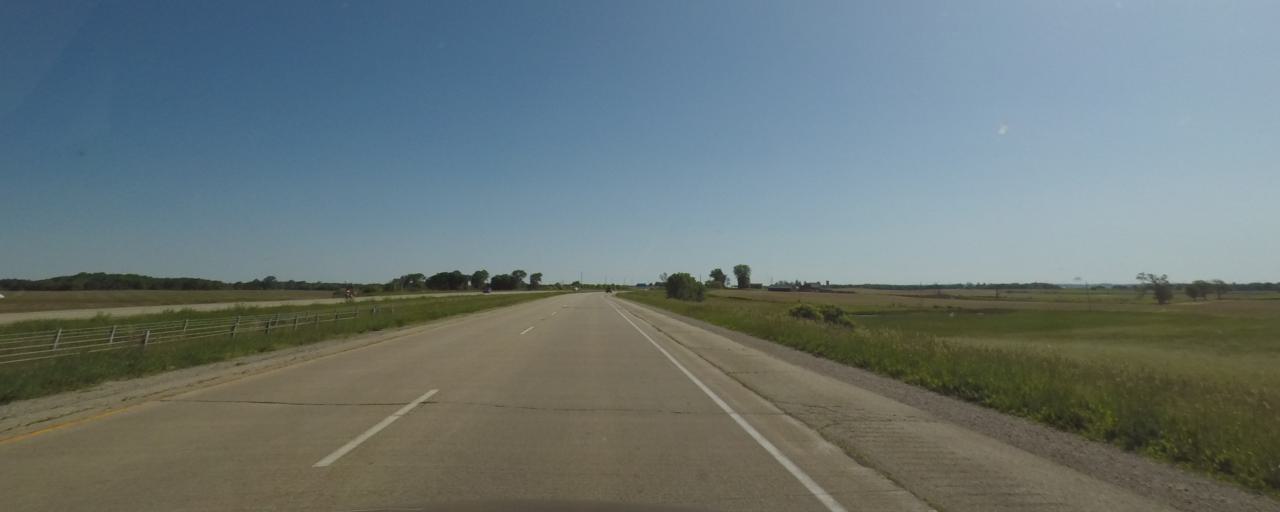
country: US
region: Wisconsin
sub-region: Fond du Lac County
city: Waupun
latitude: 43.5758
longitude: -88.7641
